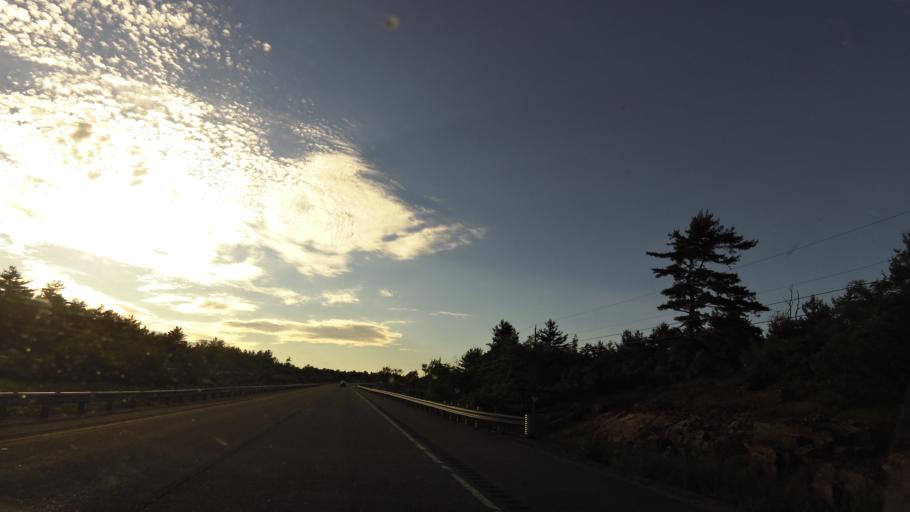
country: CA
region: Ontario
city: Midland
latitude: 44.8980
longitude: -79.7649
